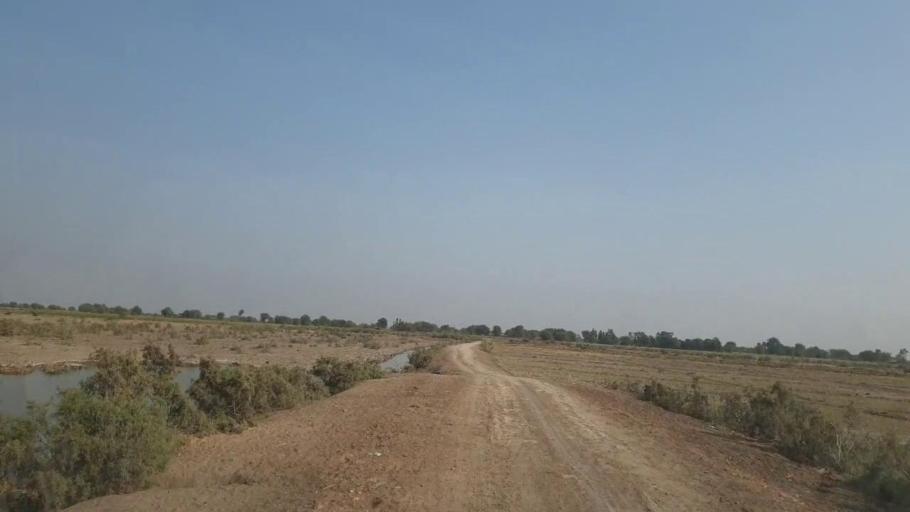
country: PK
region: Sindh
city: Pithoro
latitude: 25.6950
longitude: 69.2319
